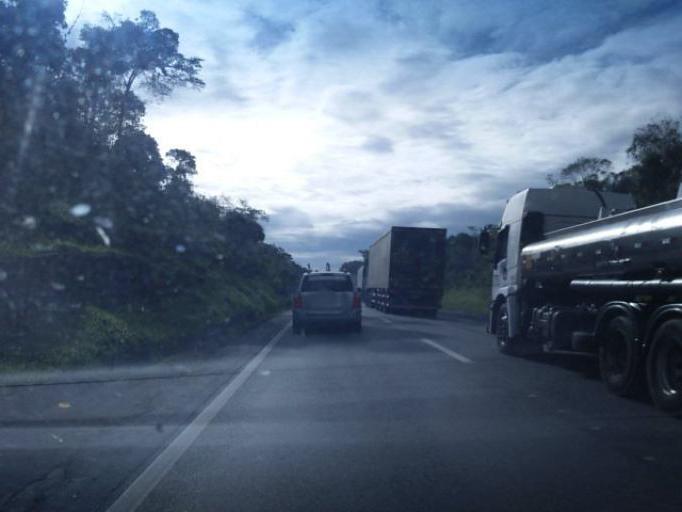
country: BR
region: Parana
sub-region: Antonina
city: Antonina
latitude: -25.1089
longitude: -48.7655
